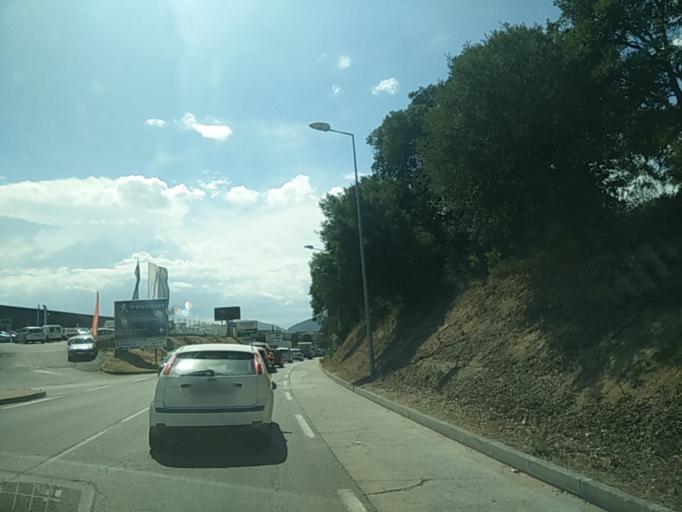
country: FR
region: Corsica
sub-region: Departement de la Corse-du-Sud
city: Afa
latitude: 41.9534
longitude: 8.7894
